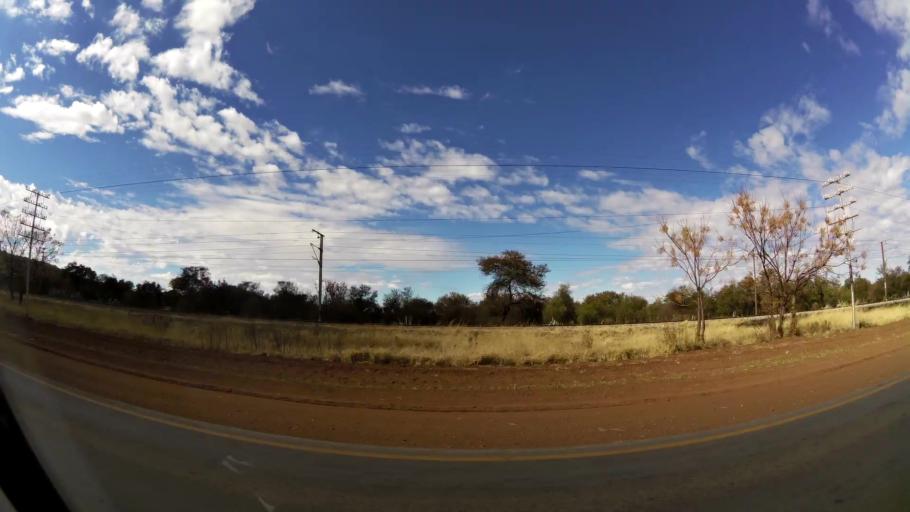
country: ZA
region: Limpopo
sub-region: Waterberg District Municipality
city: Bela-Bela
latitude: -24.8648
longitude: 28.3271
